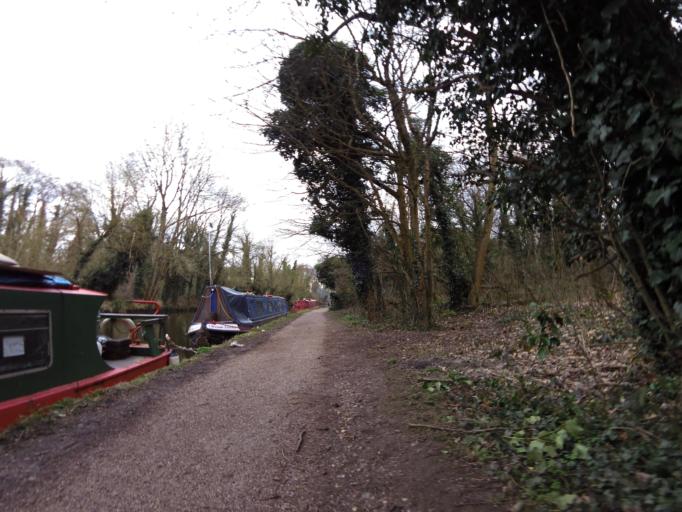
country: GB
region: England
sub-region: Hertfordshire
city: Watford
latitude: 51.6583
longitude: -0.4278
